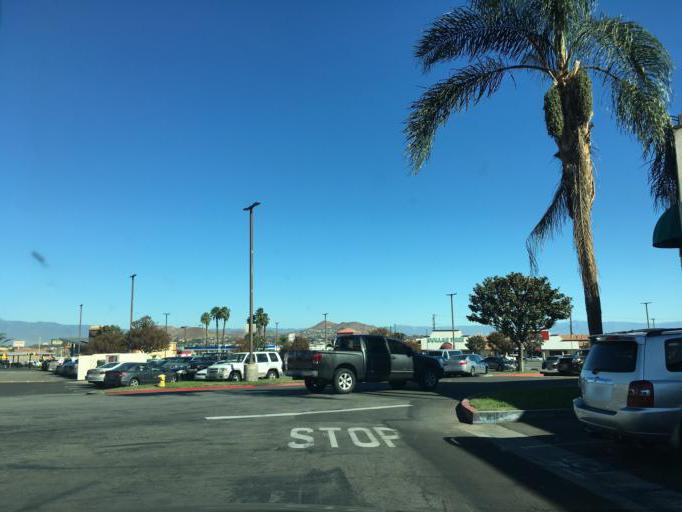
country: US
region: California
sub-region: Riverside County
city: Corona
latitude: 33.8631
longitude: -117.5441
